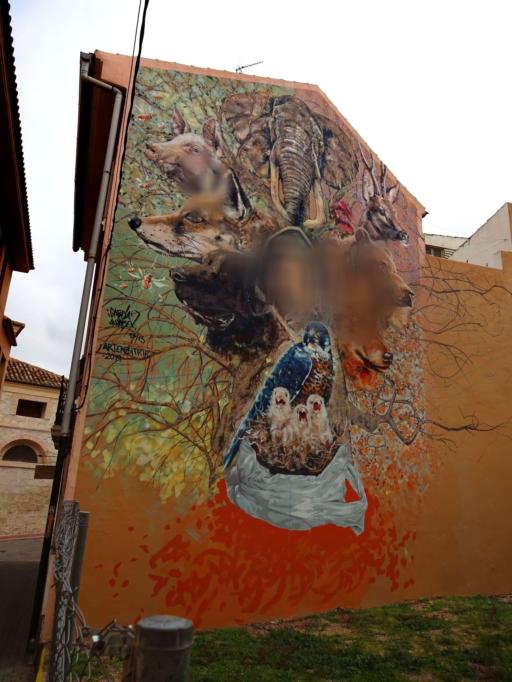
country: ES
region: Valencia
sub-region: Provincia de Alicante
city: Elda
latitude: 38.4846
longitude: -0.7695
